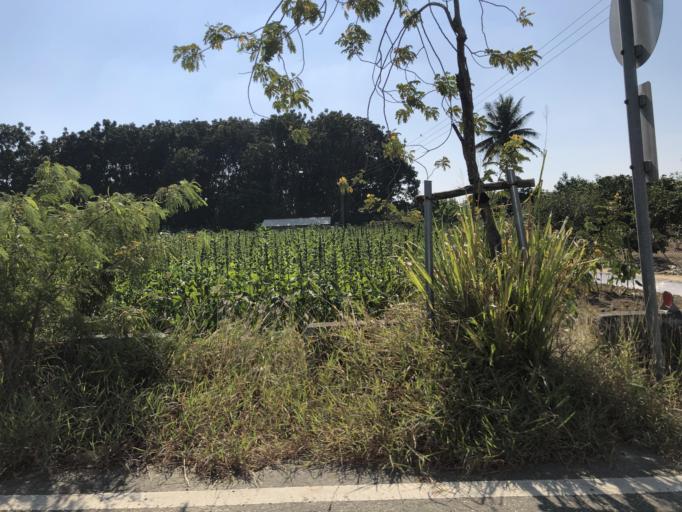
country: TW
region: Taiwan
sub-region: Tainan
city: Tainan
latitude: 23.0385
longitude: 120.3295
